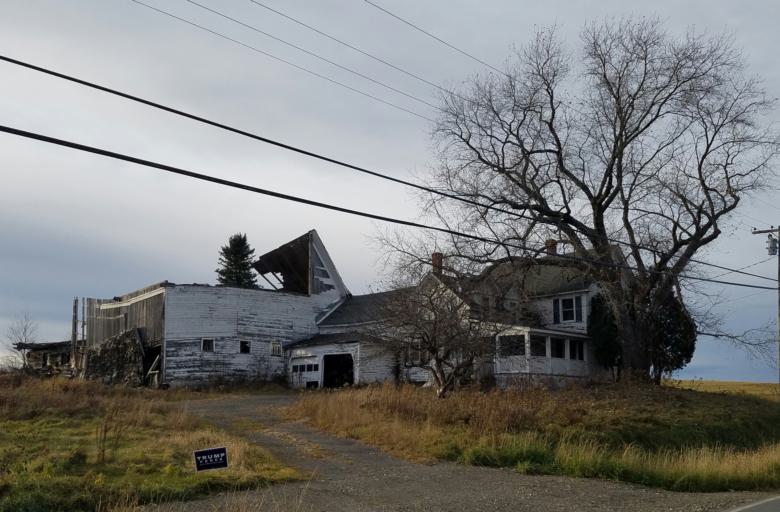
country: US
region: Maine
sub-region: Aroostook County
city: Caribou
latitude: 46.8191
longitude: -68.1662
